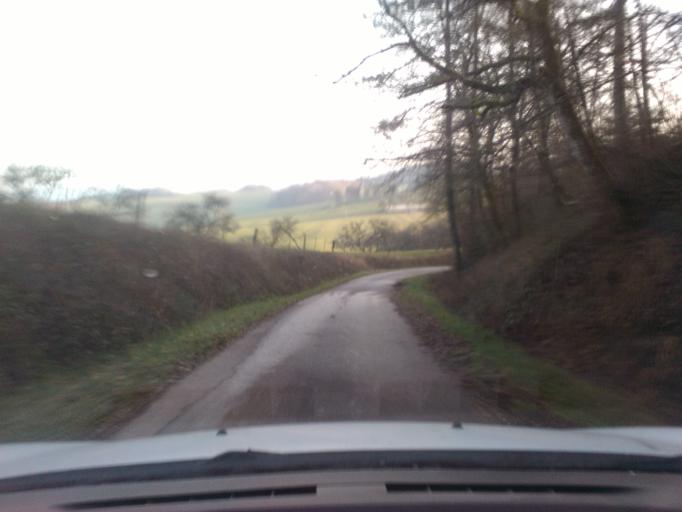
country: FR
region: Lorraine
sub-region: Departement des Vosges
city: Vittel
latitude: 48.2574
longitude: 6.0007
